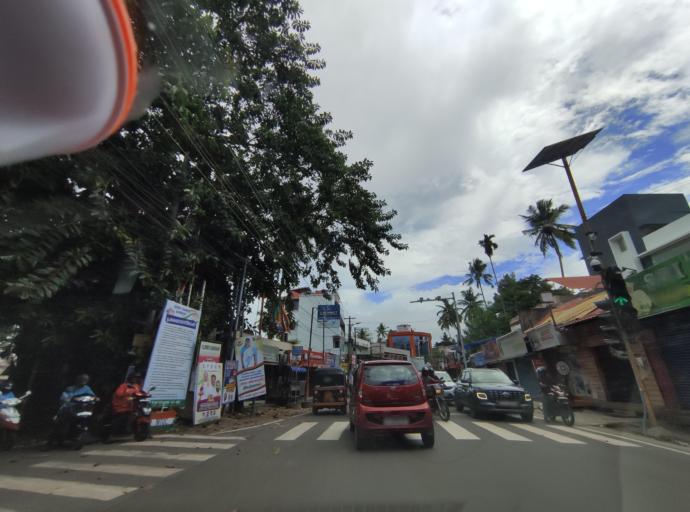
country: IN
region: Kerala
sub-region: Thiruvananthapuram
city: Thiruvananthapuram
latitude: 8.4943
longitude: 76.9646
